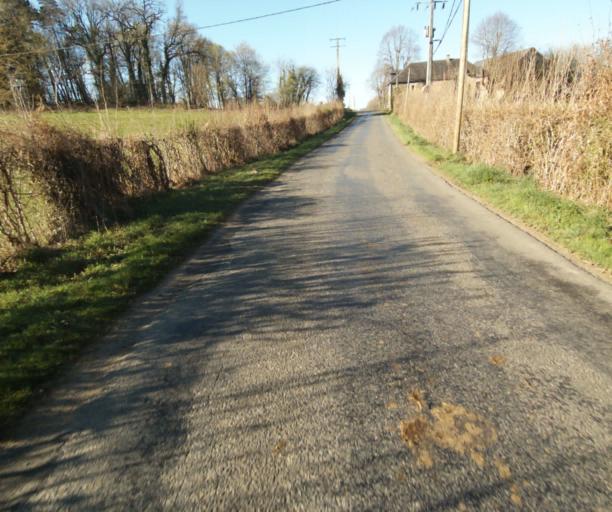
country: FR
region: Limousin
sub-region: Departement de la Correze
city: Chamboulive
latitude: 45.4086
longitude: 1.6562
